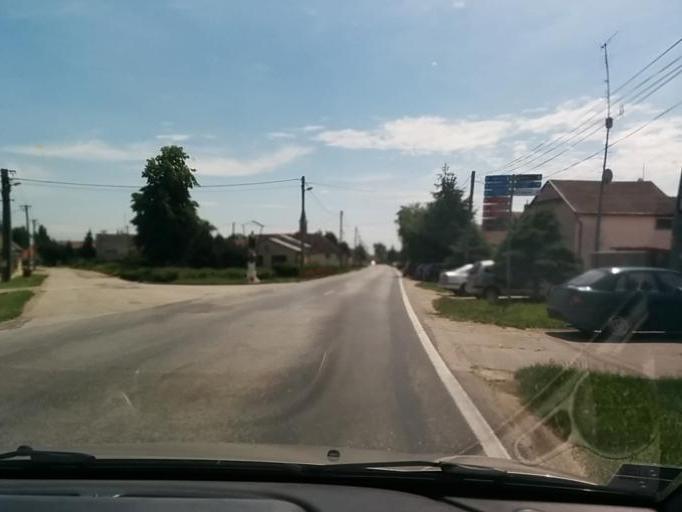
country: SK
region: Trnavsky
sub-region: Okres Galanta
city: Galanta
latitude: 48.2558
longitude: 17.8115
